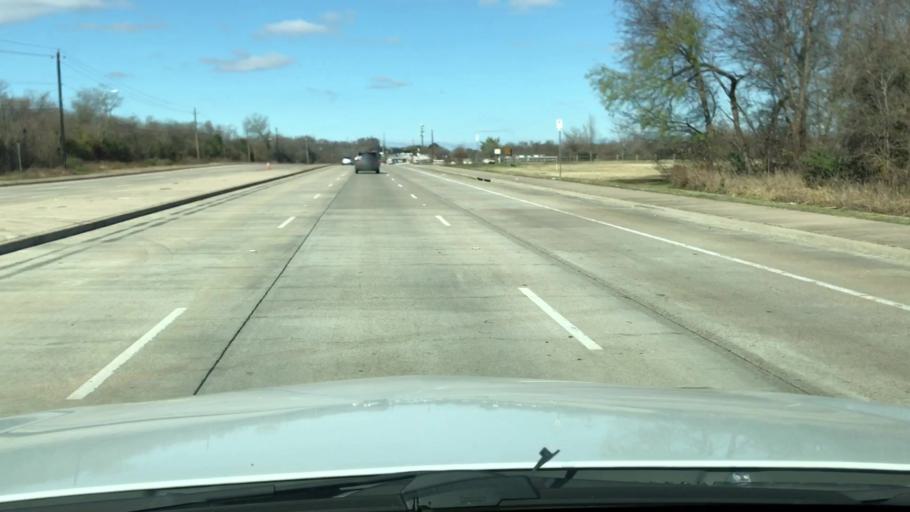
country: US
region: Texas
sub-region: Travis County
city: Onion Creek
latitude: 30.1740
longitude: -97.7420
